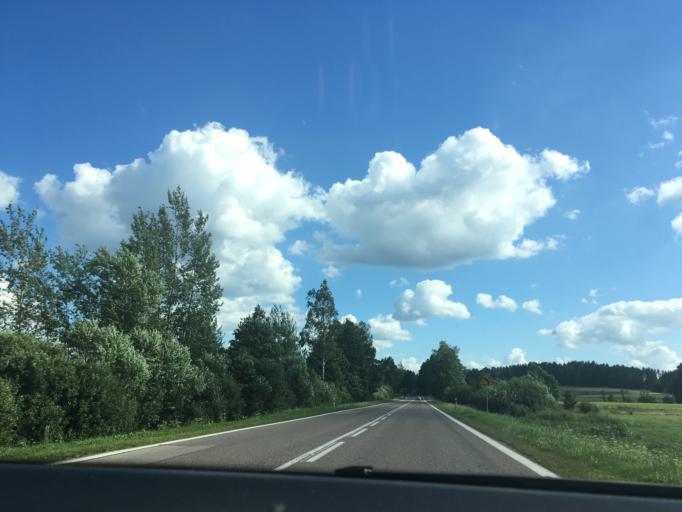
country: PL
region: Podlasie
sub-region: Powiat bialostocki
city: Dobrzyniewo Duze
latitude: 53.3424
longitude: 23.1004
